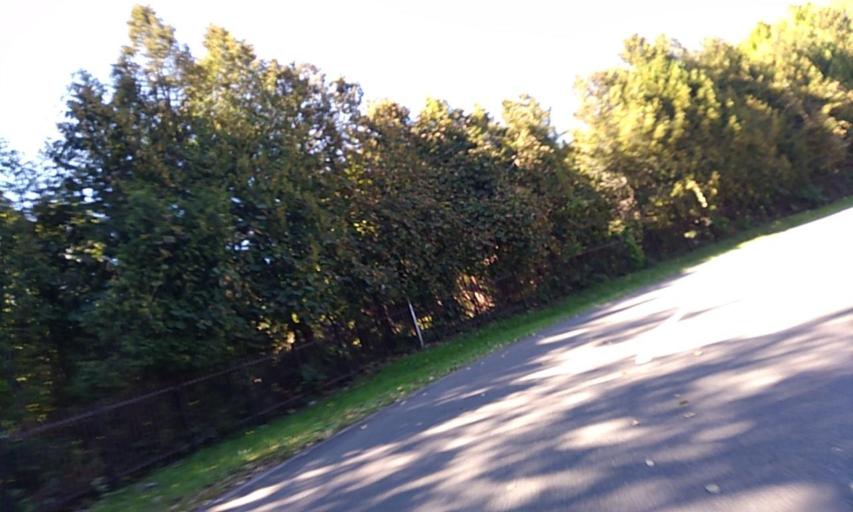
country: JP
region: Hokkaido
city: Sapporo
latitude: 42.9974
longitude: 141.3930
